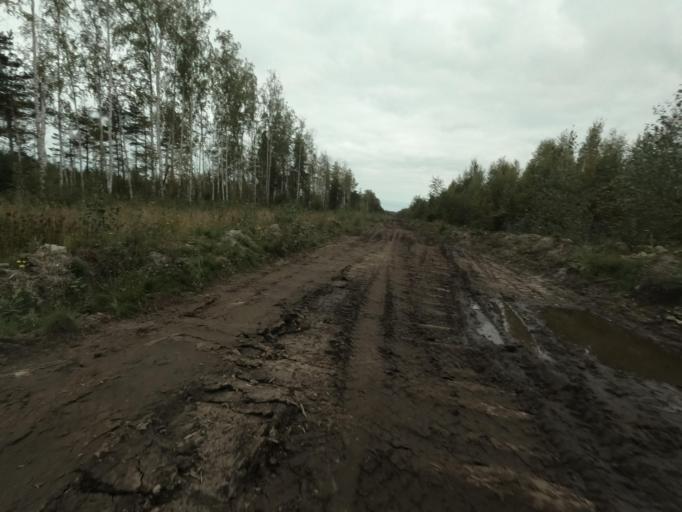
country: RU
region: St.-Petersburg
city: Sapernyy
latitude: 59.7591
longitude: 30.7135
